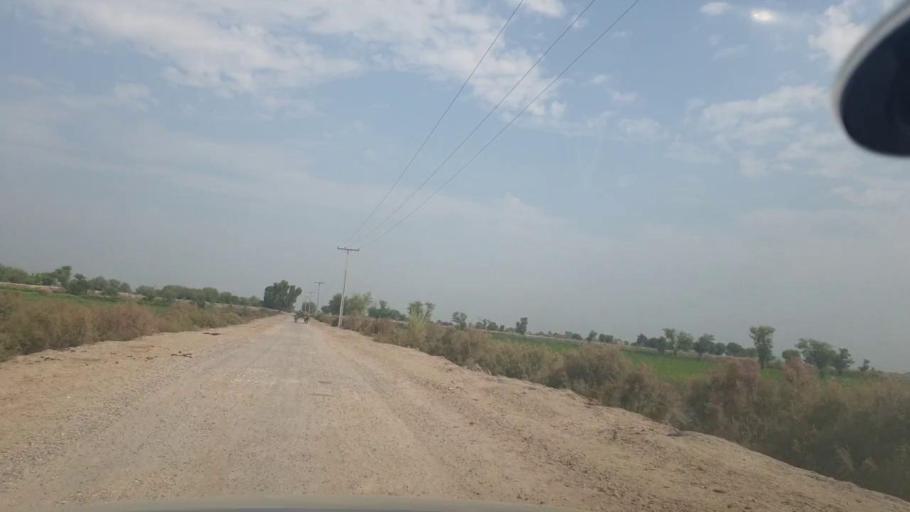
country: PK
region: Balochistan
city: Mehrabpur
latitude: 28.0592
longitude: 68.1054
